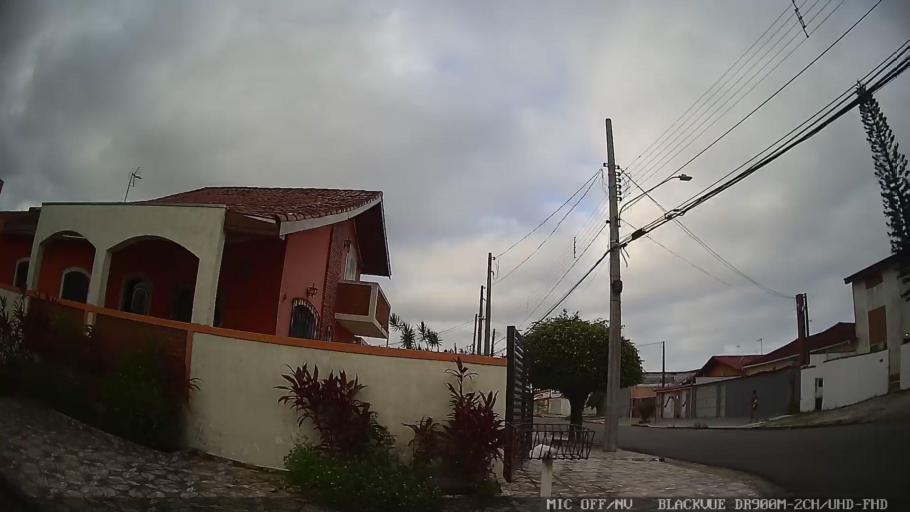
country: BR
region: Sao Paulo
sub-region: Peruibe
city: Peruibe
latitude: -24.3103
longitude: -46.9923
